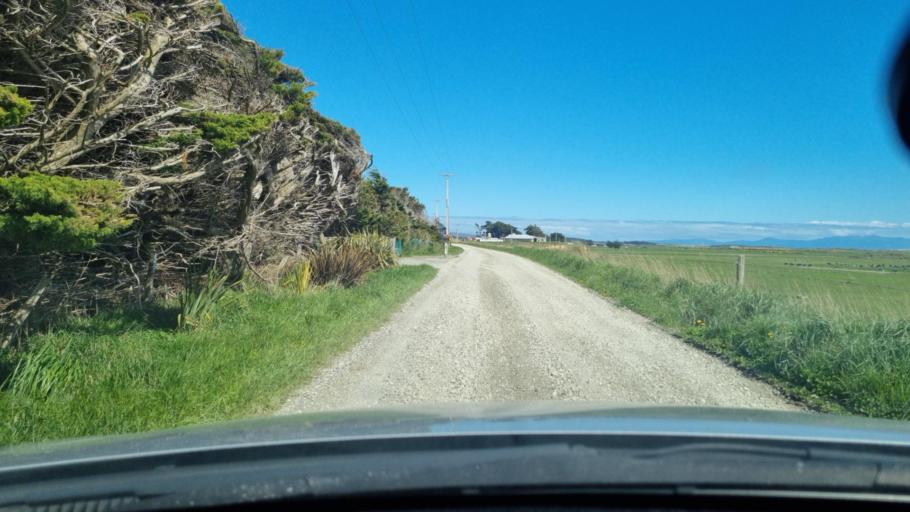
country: NZ
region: Southland
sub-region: Invercargill City
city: Invercargill
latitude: -46.3950
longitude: 168.2578
